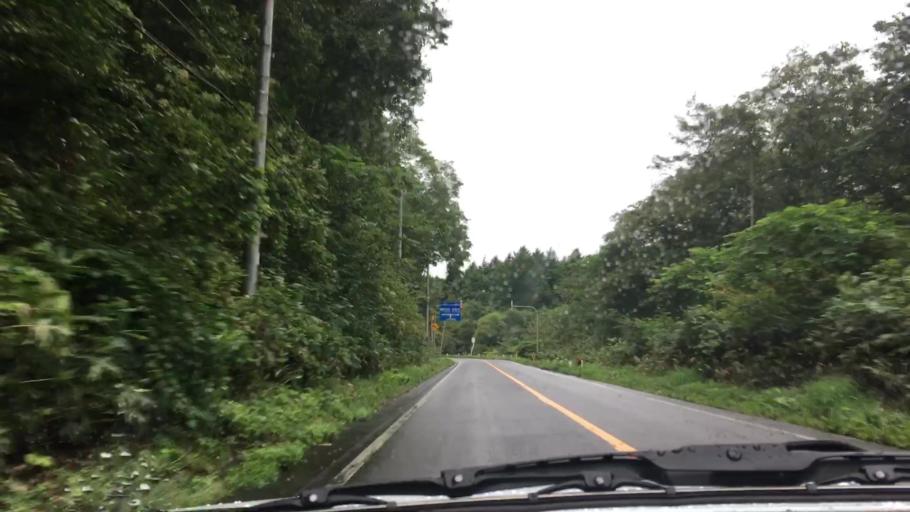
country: JP
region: Hokkaido
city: Niseko Town
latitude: 42.6125
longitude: 140.7279
